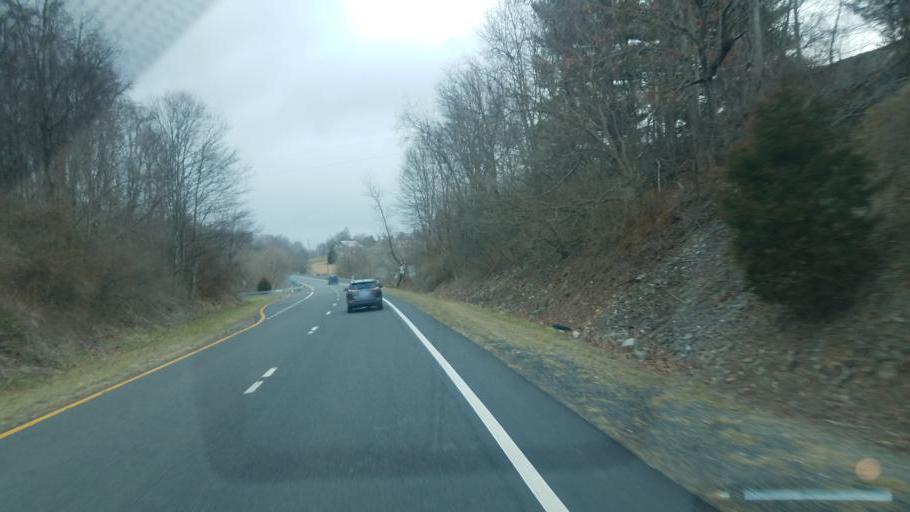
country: US
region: Virginia
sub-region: Giles County
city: Pearisburg
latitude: 37.2894
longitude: -80.7414
